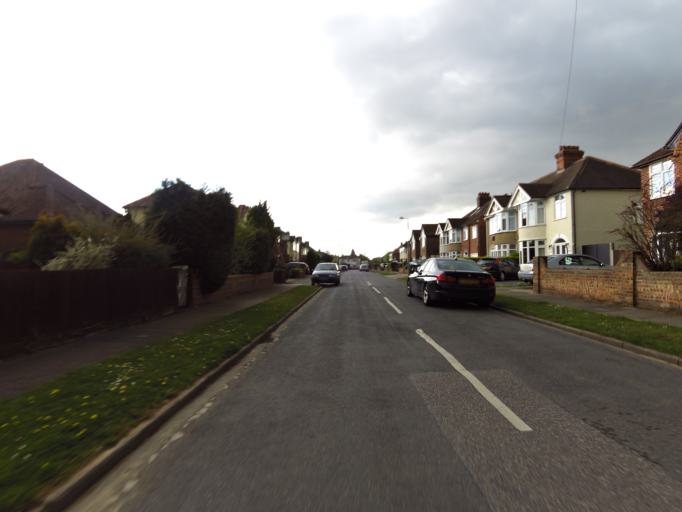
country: GB
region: England
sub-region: Suffolk
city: Kesgrave
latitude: 52.0605
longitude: 1.2034
